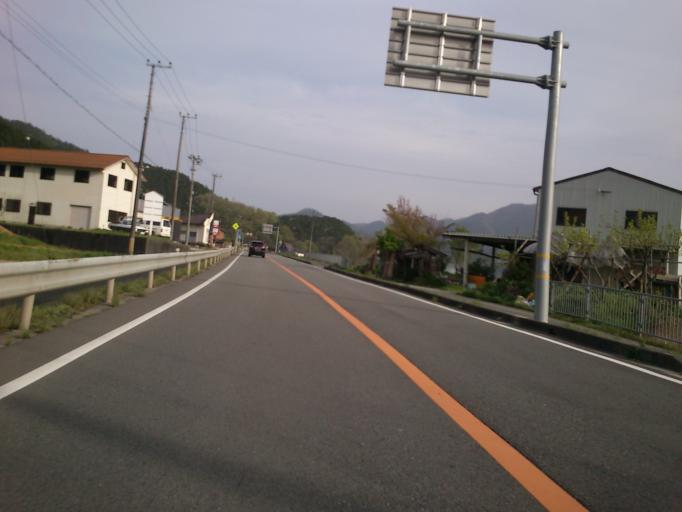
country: JP
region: Hyogo
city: Sasayama
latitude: 35.0899
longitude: 135.3158
